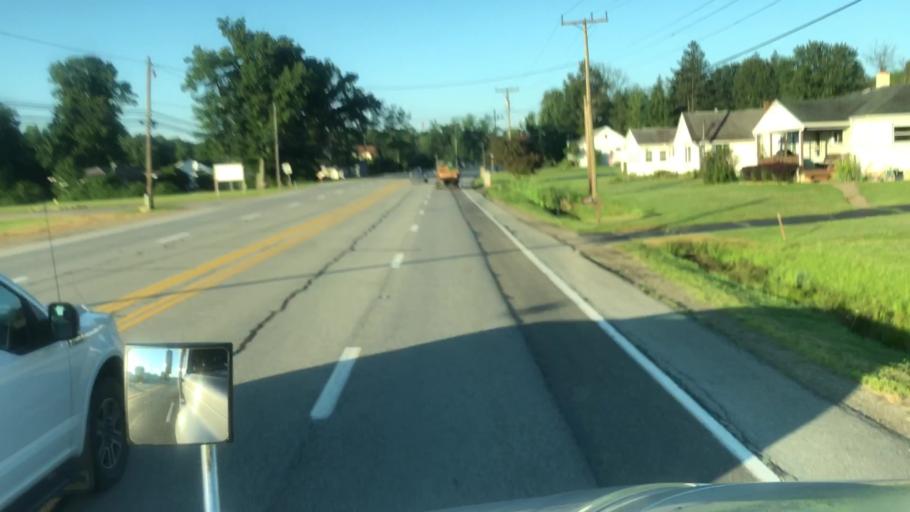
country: US
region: Pennsylvania
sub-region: Venango County
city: Franklin
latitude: 41.3722
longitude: -79.8564
